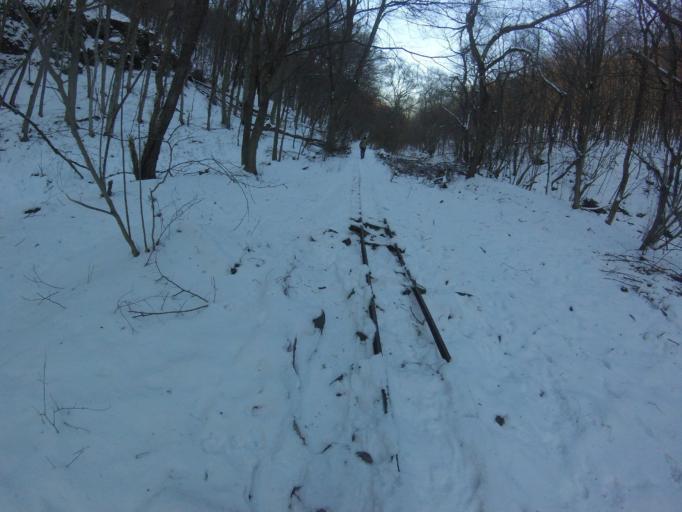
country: SK
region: Nitriansky
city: Sahy
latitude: 47.9770
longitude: 18.8949
